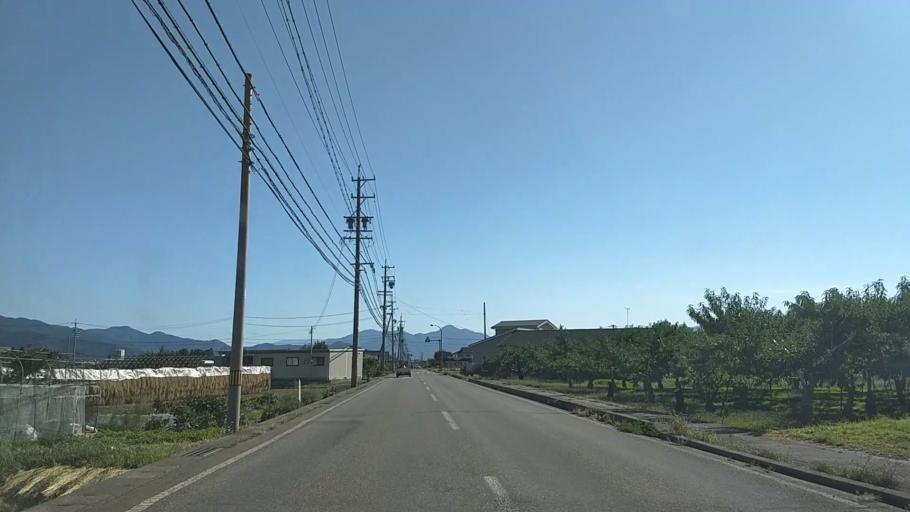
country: JP
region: Nagano
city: Nagano-shi
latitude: 36.6089
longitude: 138.1437
